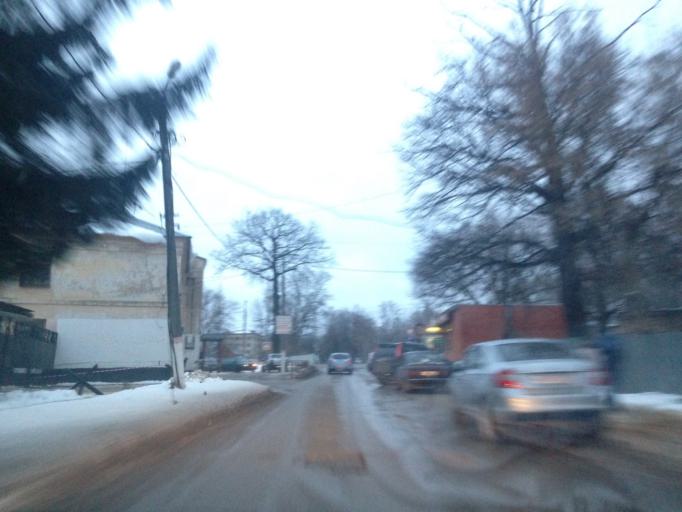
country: RU
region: Tula
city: Shchekino
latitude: 53.9987
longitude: 37.5108
